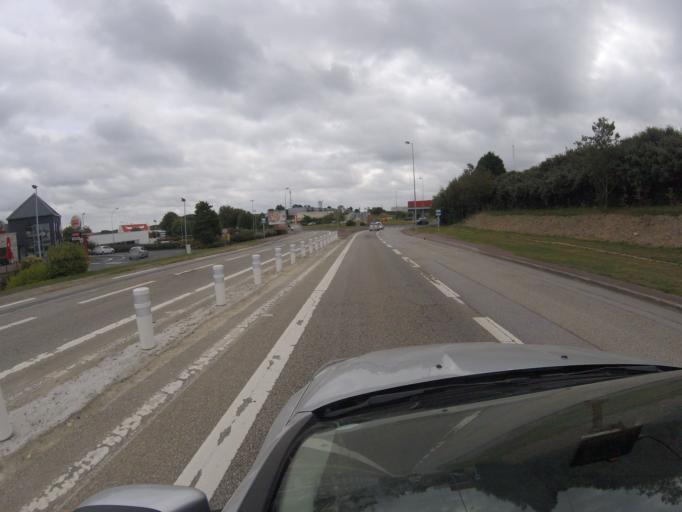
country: FR
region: Lower Normandy
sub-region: Departement de la Manche
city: La Glacerie
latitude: 49.6061
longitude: -1.5992
